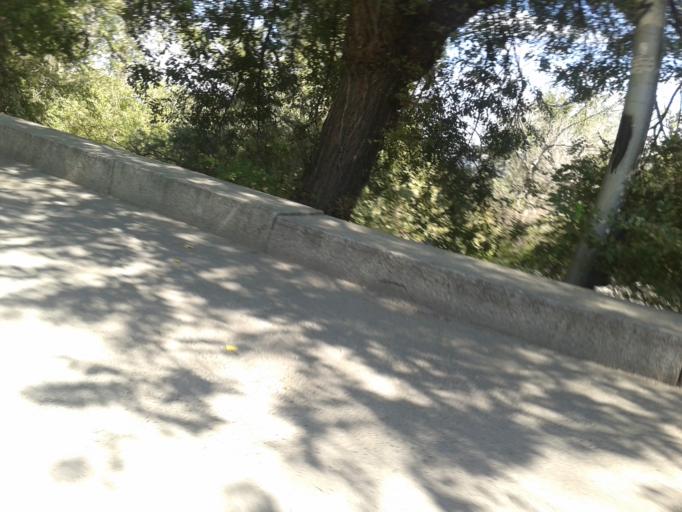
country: RU
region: Volgograd
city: Volgograd
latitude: 48.7071
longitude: 44.5254
